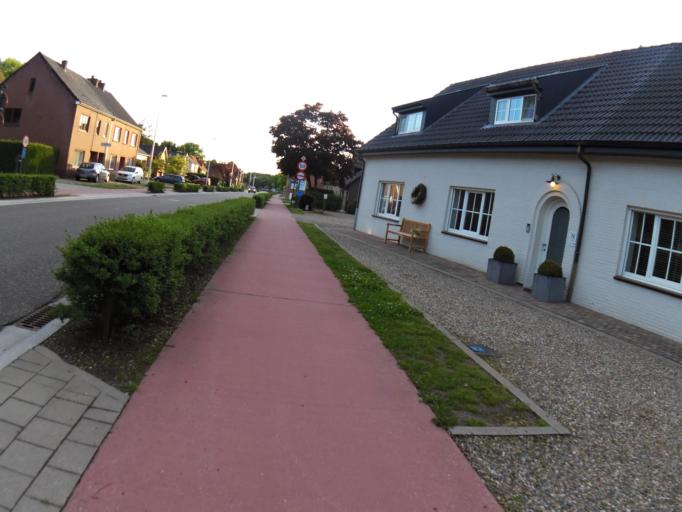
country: BE
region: Flanders
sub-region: Provincie Limburg
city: Zutendaal
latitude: 50.9353
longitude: 5.5813
